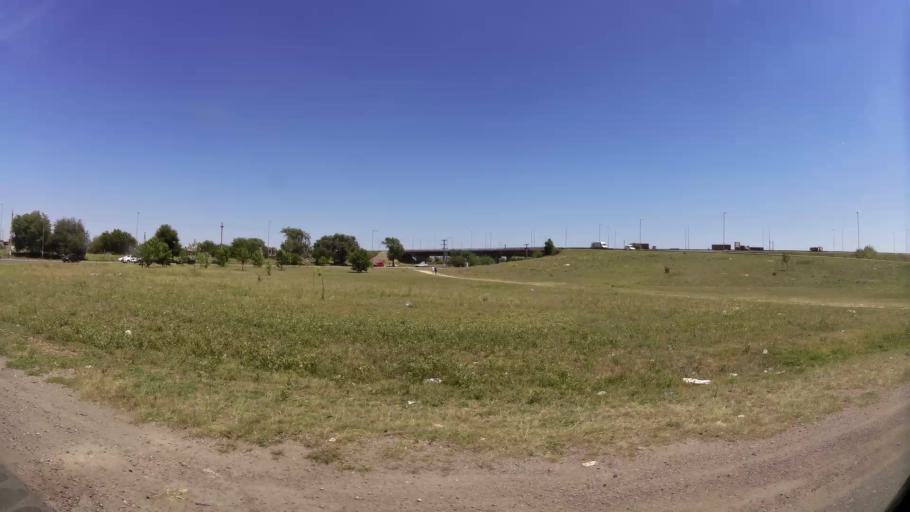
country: AR
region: Cordoba
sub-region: Departamento de Capital
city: Cordoba
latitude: -31.4445
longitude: -64.1224
